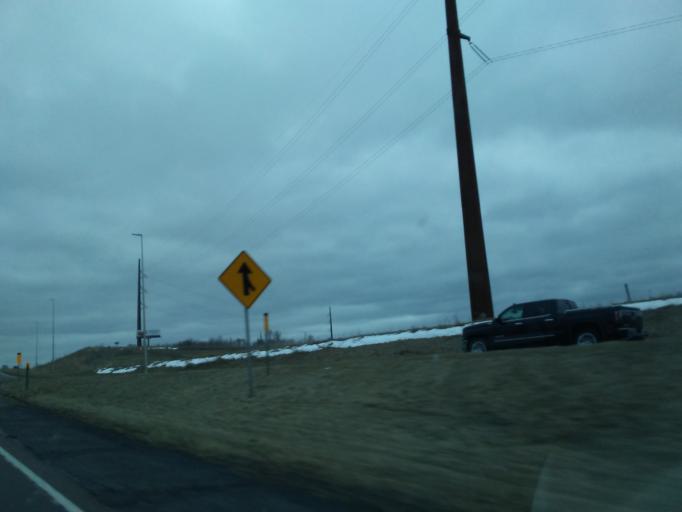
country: US
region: Minnesota
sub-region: Goodhue County
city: Cannon Falls
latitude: 44.6031
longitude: -92.9942
